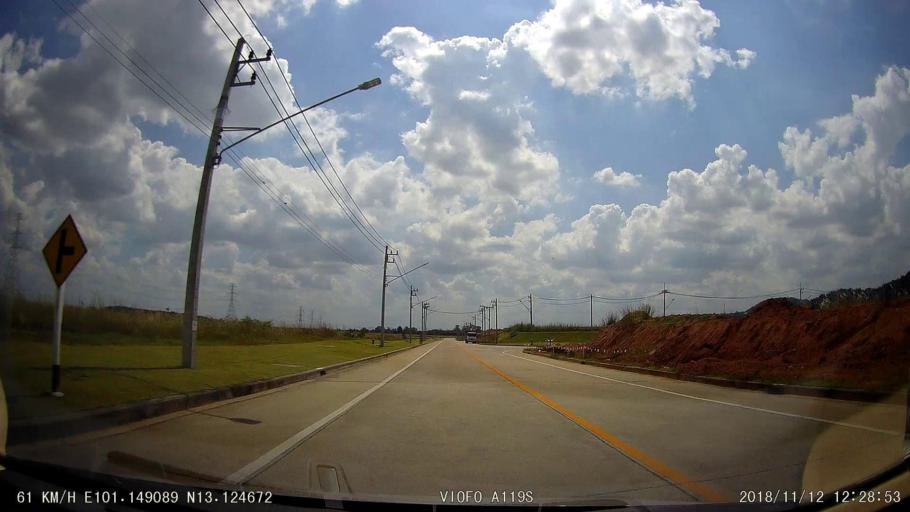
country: TH
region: Chon Buri
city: Ban Talat Bueng
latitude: 13.1242
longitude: 101.1491
